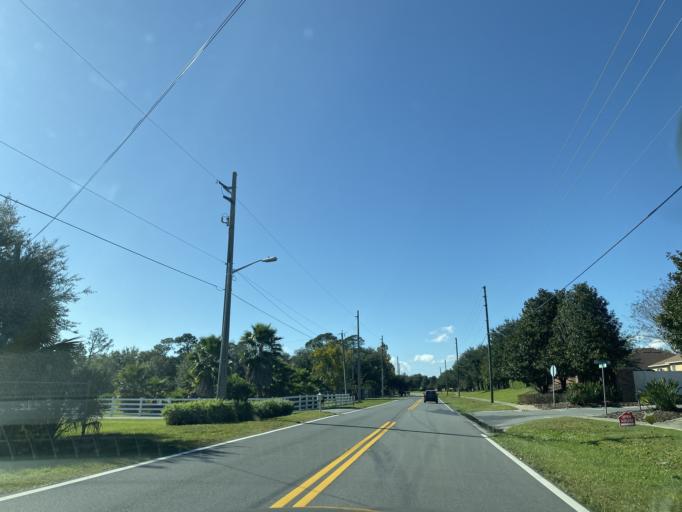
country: US
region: Florida
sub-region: Orange County
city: Meadow Woods
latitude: 28.4000
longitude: -81.2373
